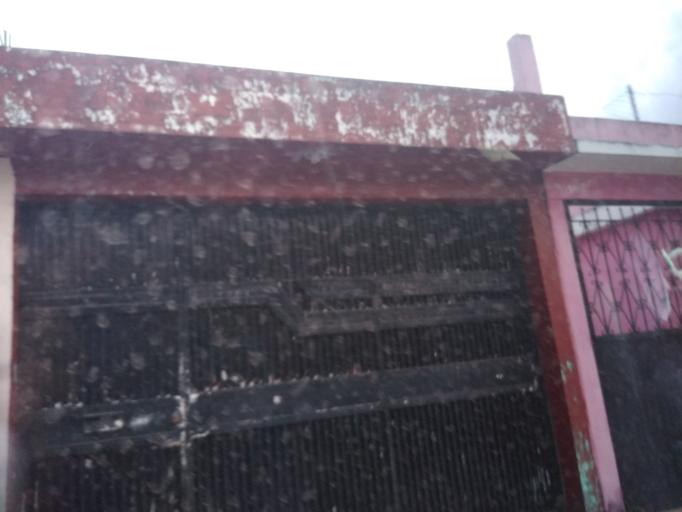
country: GT
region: Guatemala
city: Petapa
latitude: 14.5076
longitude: -90.5591
